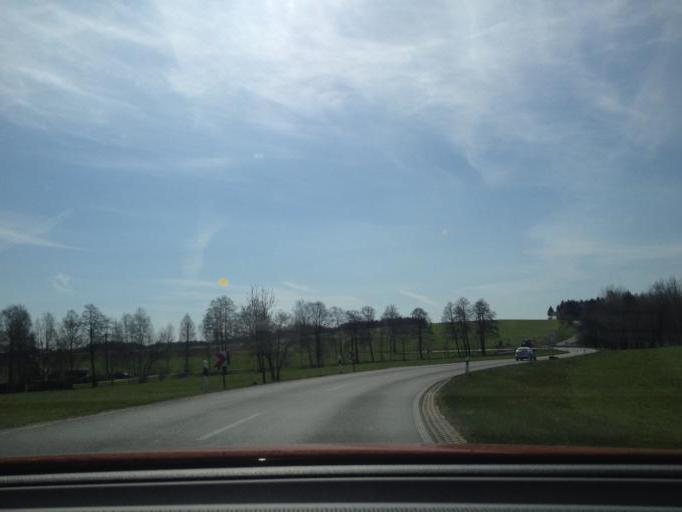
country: DE
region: Bavaria
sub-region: Upper Franconia
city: Weissenstadt
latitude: 50.0928
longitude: 11.8962
